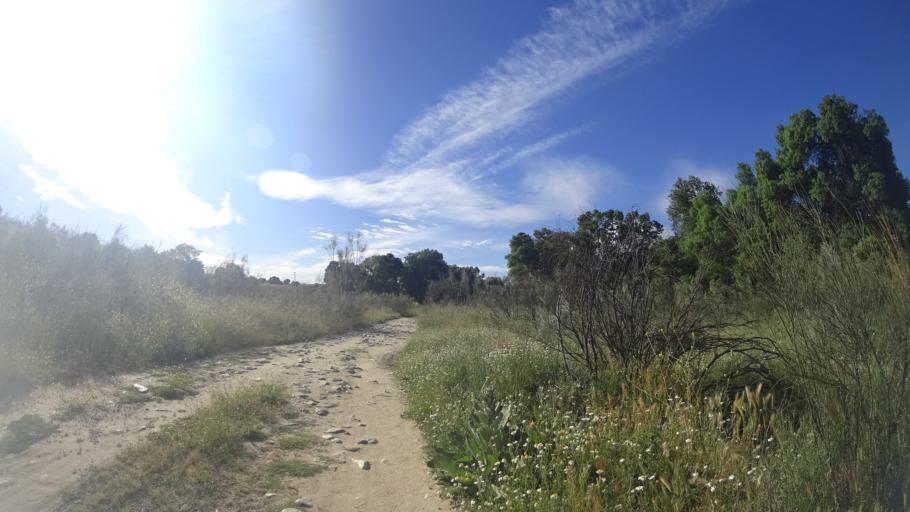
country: ES
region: Madrid
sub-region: Provincia de Madrid
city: Villanueva del Pardillo
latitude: 40.5146
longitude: -3.9410
